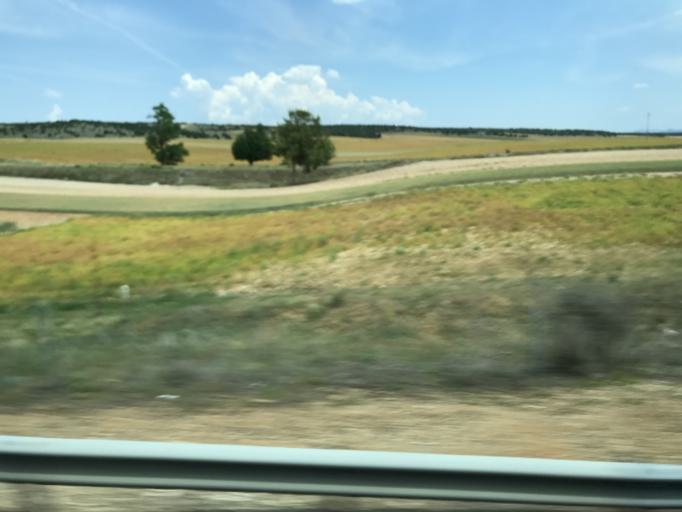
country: ES
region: Castille and Leon
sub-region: Provincia de Burgos
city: Fontioso
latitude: 41.9531
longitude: -3.7662
